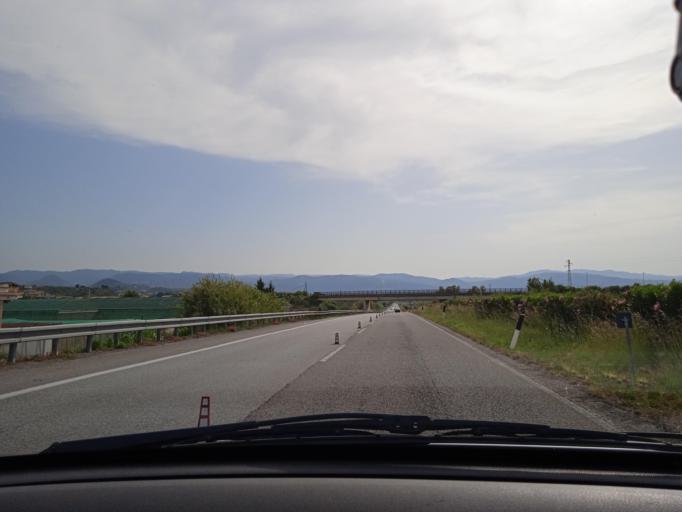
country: IT
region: Sicily
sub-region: Messina
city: Terme
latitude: 38.1428
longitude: 15.1630
